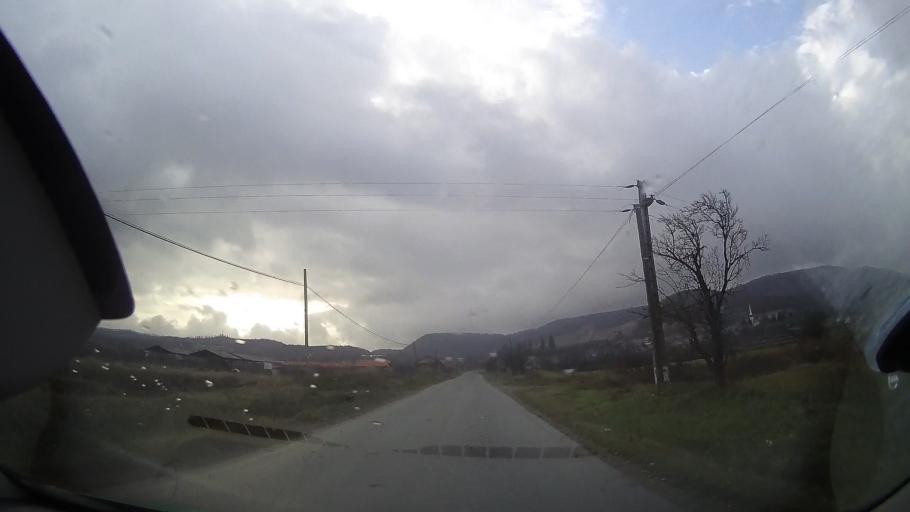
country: RO
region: Cluj
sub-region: Comuna Moldovenesti
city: Moldovenesti
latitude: 46.5053
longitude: 23.6674
